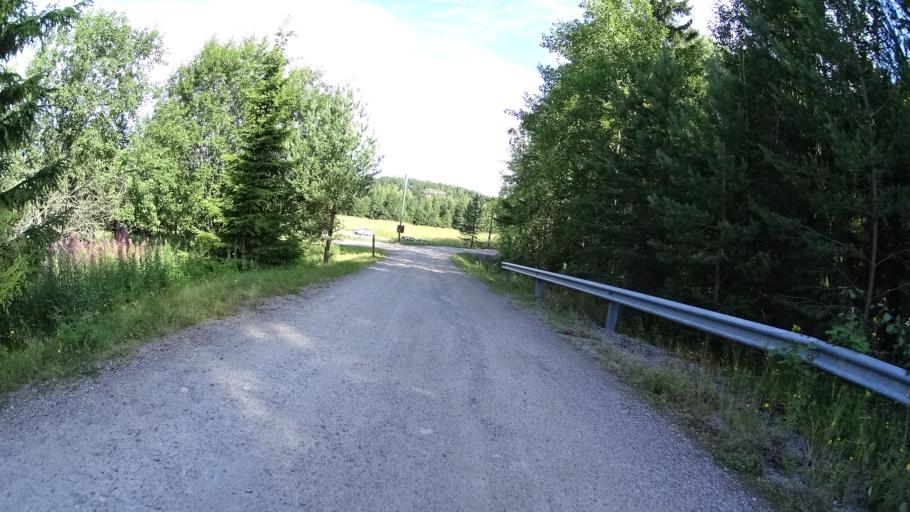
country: FI
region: Uusimaa
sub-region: Helsinki
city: Kirkkonummi
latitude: 60.1143
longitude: 24.4451
